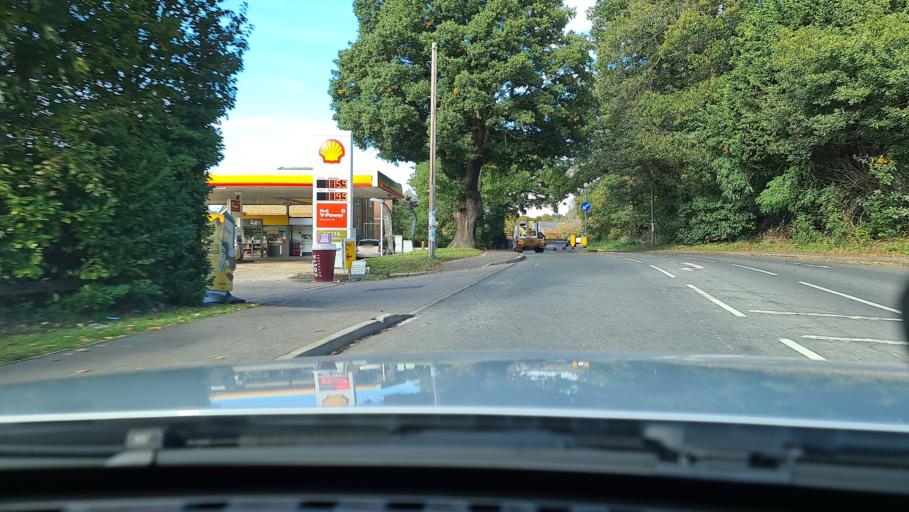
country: GB
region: England
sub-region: Surrey
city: Byfleet
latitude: 51.3461
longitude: -0.4628
